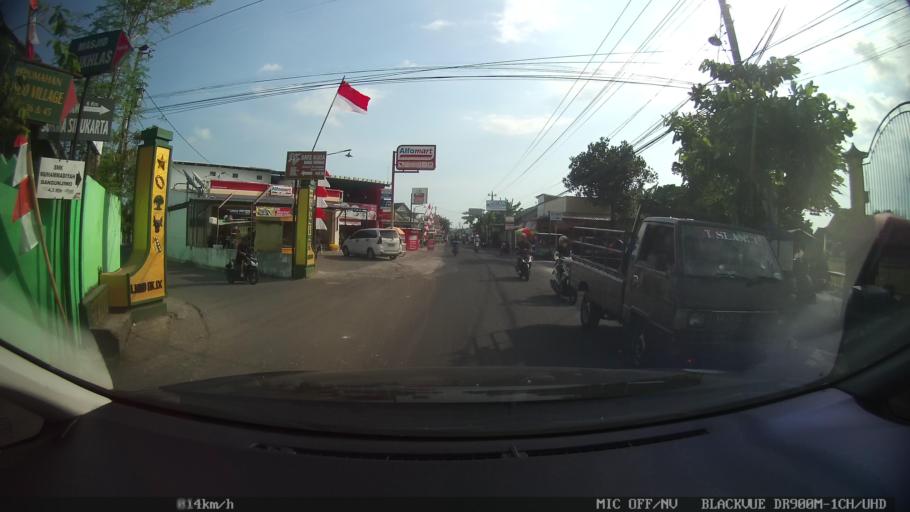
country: ID
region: Daerah Istimewa Yogyakarta
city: Kasihan
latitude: -7.8256
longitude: 110.3282
